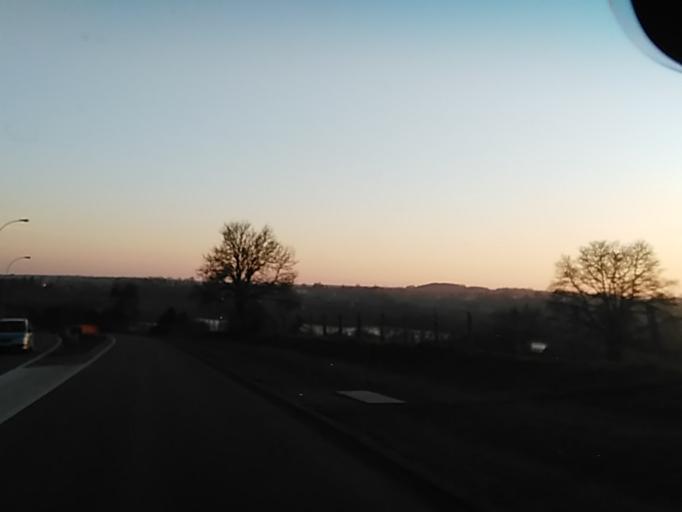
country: FR
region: Lower Normandy
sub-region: Departement de l'Orne
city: La Ferte-Mace
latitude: 48.5950
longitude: -0.3655
